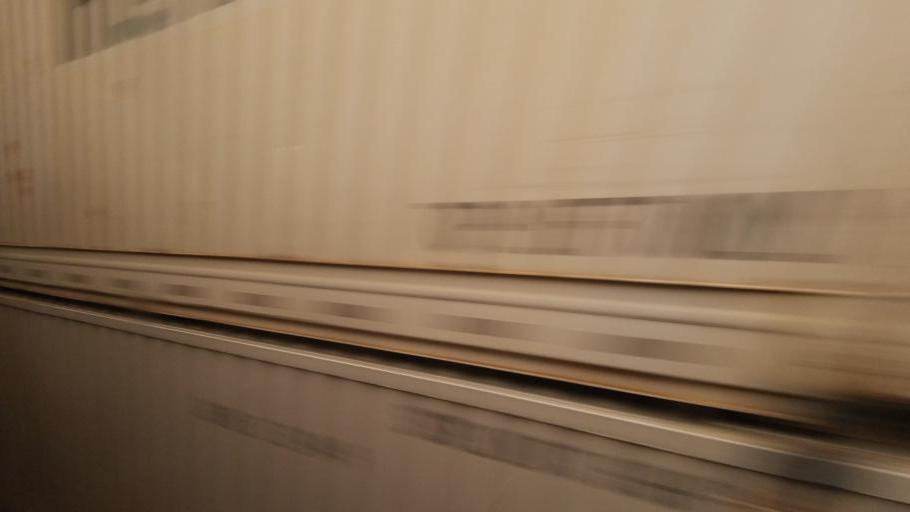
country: US
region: Arizona
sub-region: Coconino County
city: Parks
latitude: 35.2451
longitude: -111.9717
